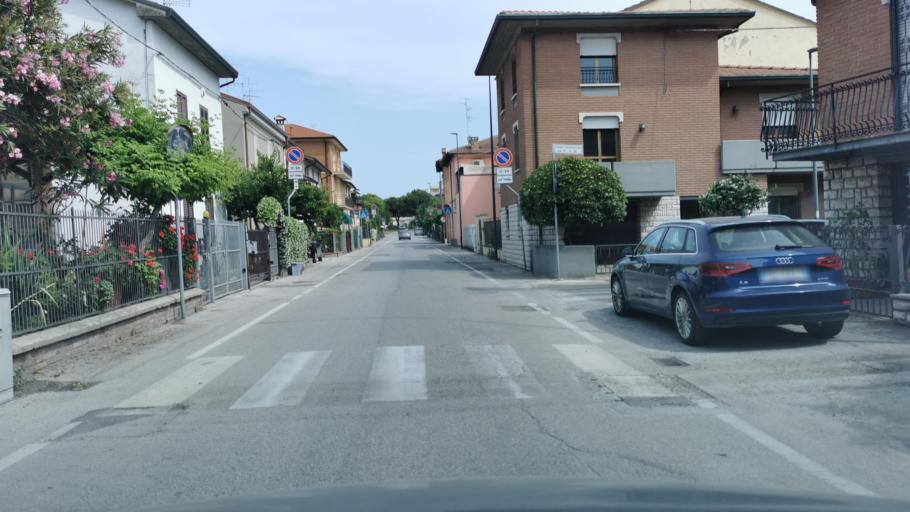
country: IT
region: Emilia-Romagna
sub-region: Provincia di Ravenna
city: Ravenna
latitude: 44.4157
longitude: 12.1859
